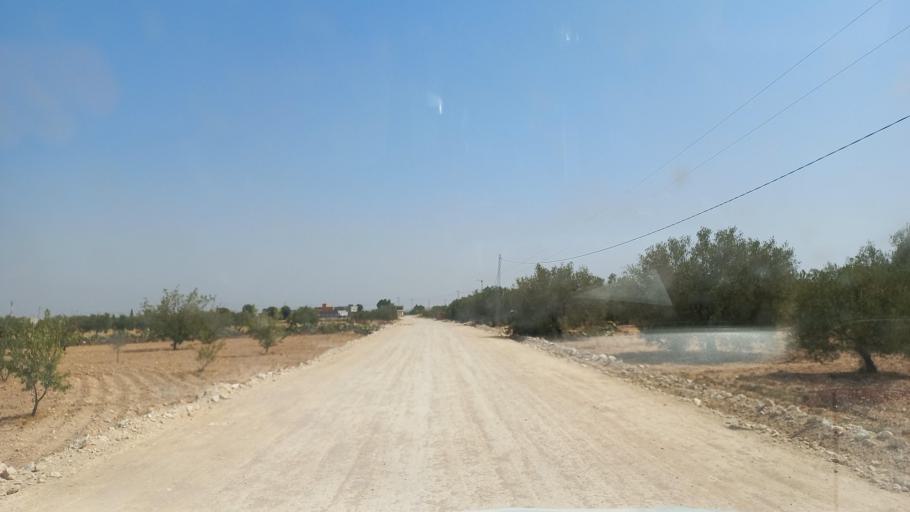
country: TN
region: Al Qasrayn
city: Kasserine
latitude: 35.2571
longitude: 9.0136
